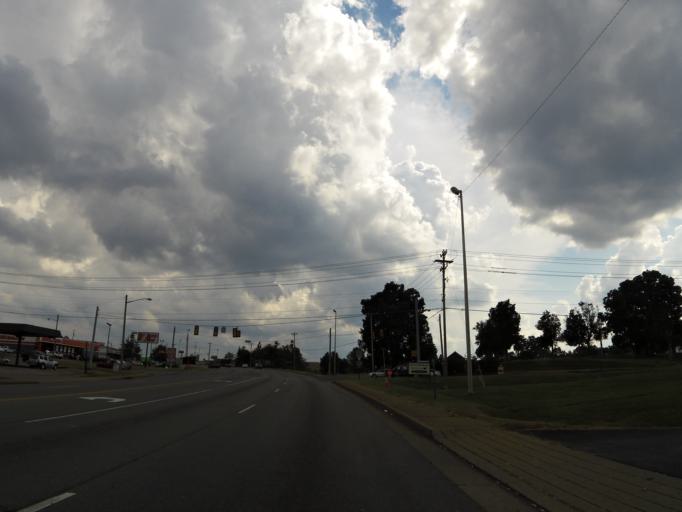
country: US
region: Tennessee
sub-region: Dickson County
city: Dickson
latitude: 36.0696
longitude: -87.3808
